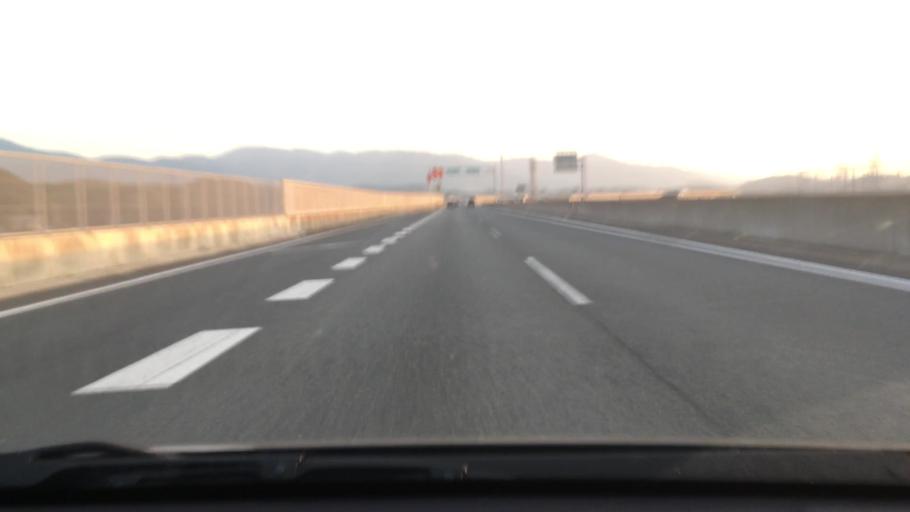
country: JP
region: Fukuoka
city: Maebaru-chuo
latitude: 33.5700
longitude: 130.2494
